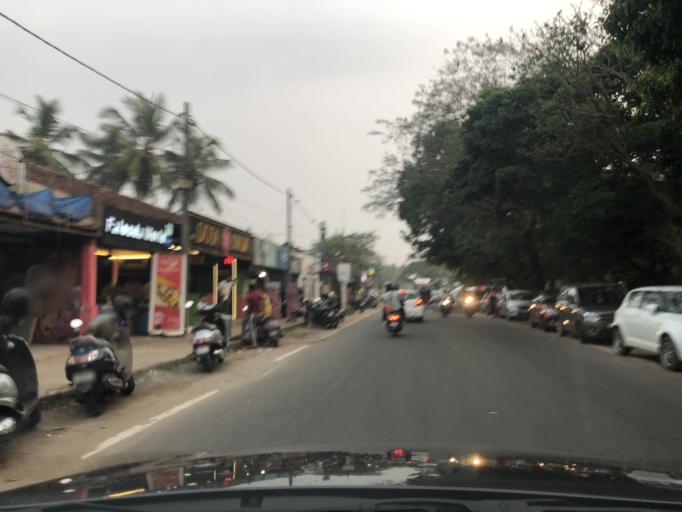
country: IN
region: Kerala
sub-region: Kozhikode
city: Kozhikode
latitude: 11.2607
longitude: 75.7687
